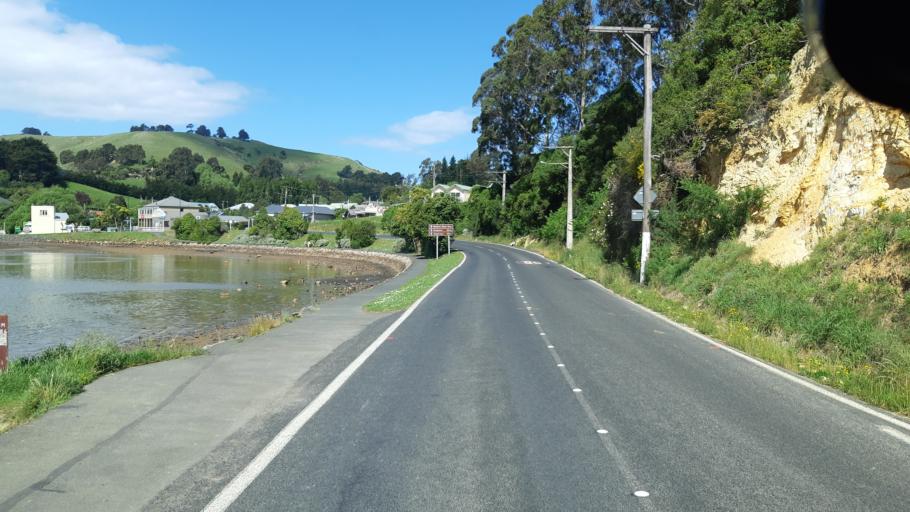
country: NZ
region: Otago
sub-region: Dunedin City
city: Portobello
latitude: -45.8391
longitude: 170.6483
